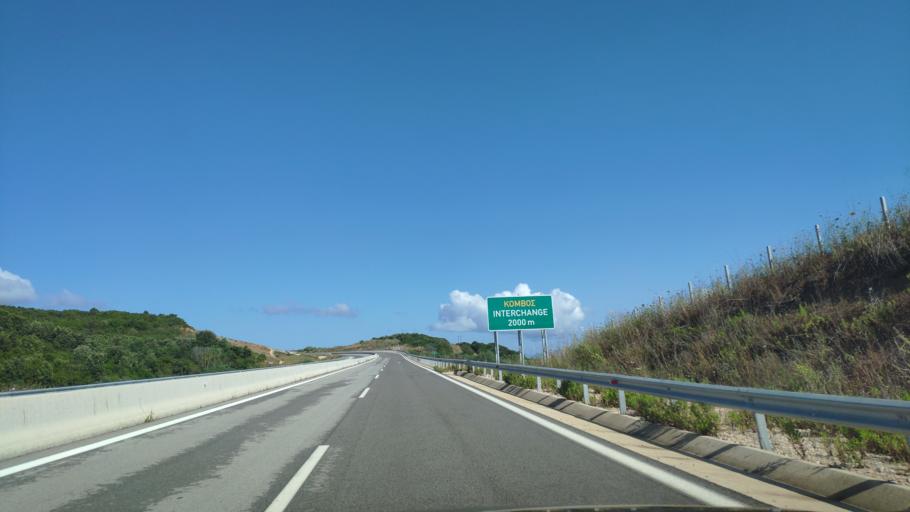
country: GR
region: West Greece
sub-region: Nomos Aitolias kai Akarnanias
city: Vonitsa
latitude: 38.9127
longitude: 20.8286
